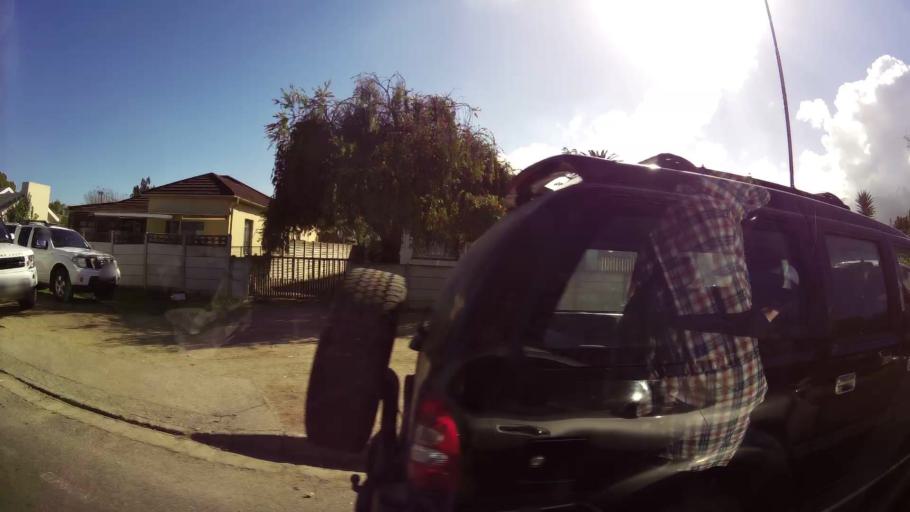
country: ZA
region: Western Cape
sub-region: Eden District Municipality
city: George
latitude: -33.9677
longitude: 22.4541
